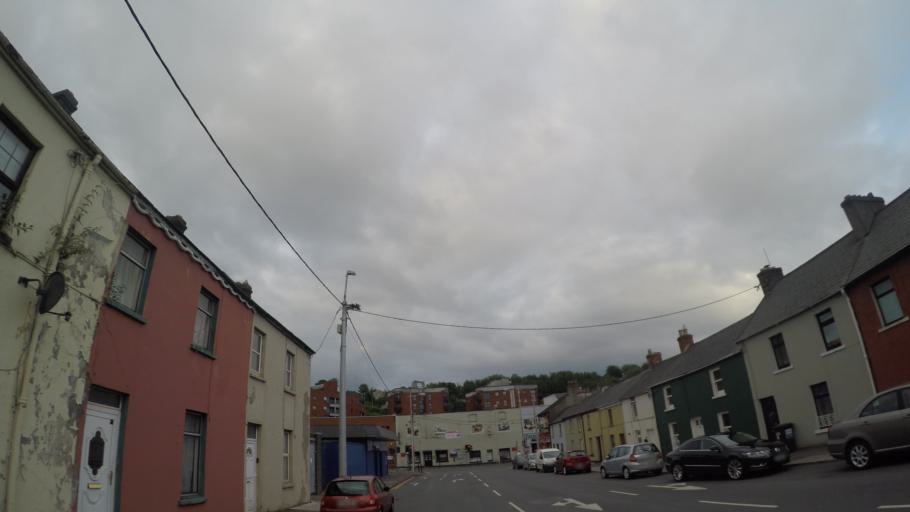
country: IE
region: Munster
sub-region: County Cork
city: Cork
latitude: 51.9140
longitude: -8.4816
